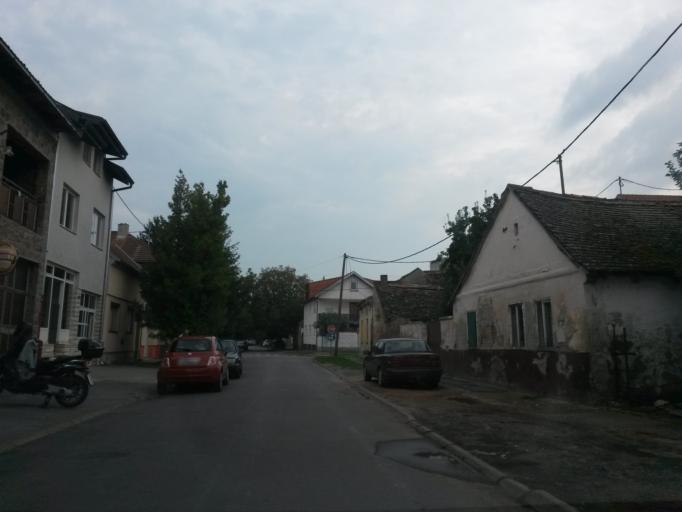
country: HR
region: Osjecko-Baranjska
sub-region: Grad Osijek
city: Osijek
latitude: 45.5579
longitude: 18.7233
